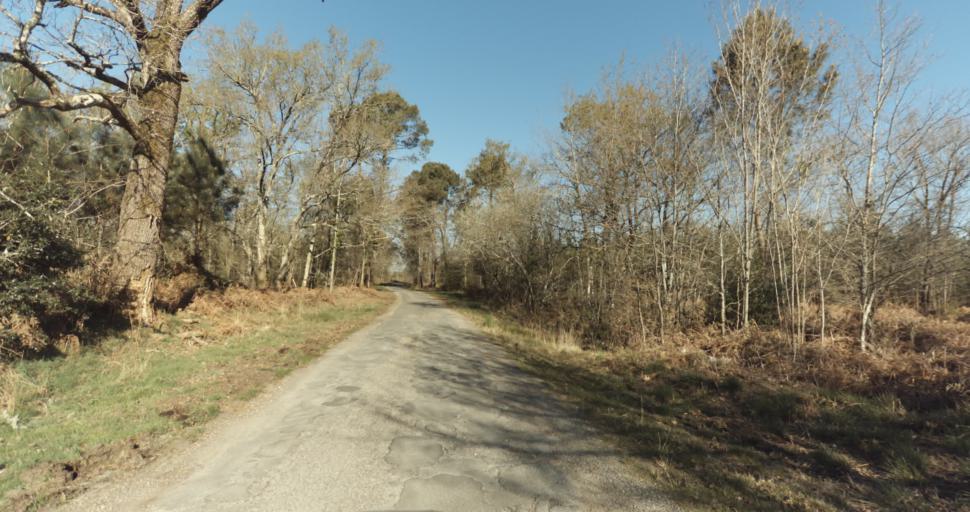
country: FR
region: Aquitaine
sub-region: Departement de la Gironde
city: Martignas-sur-Jalle
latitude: 44.8062
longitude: -0.8458
